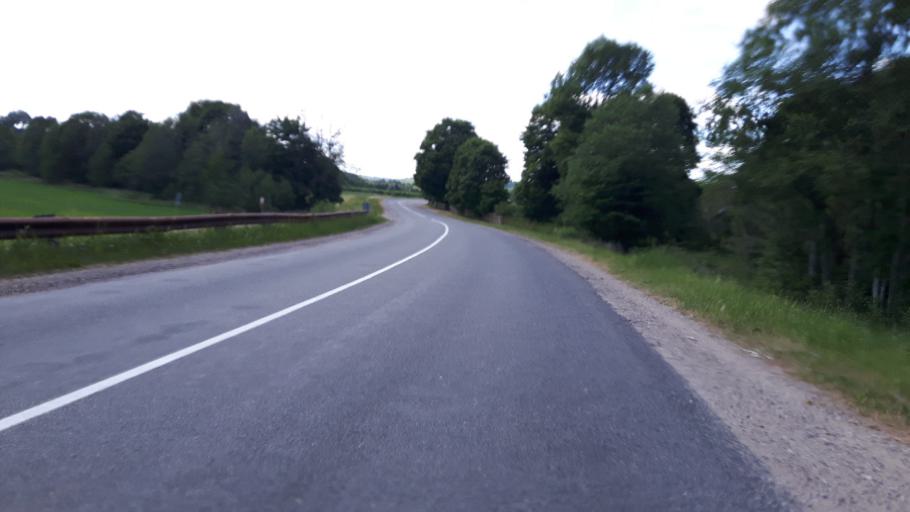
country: LV
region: Kandava
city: Kandava
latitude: 57.0249
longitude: 22.6938
